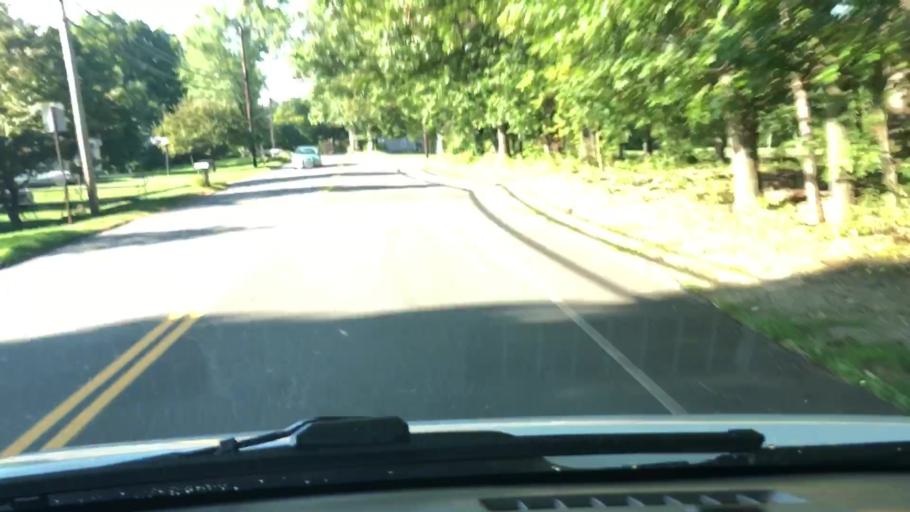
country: US
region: Massachusetts
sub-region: Franklin County
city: Greenfield
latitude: 42.6163
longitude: -72.6114
